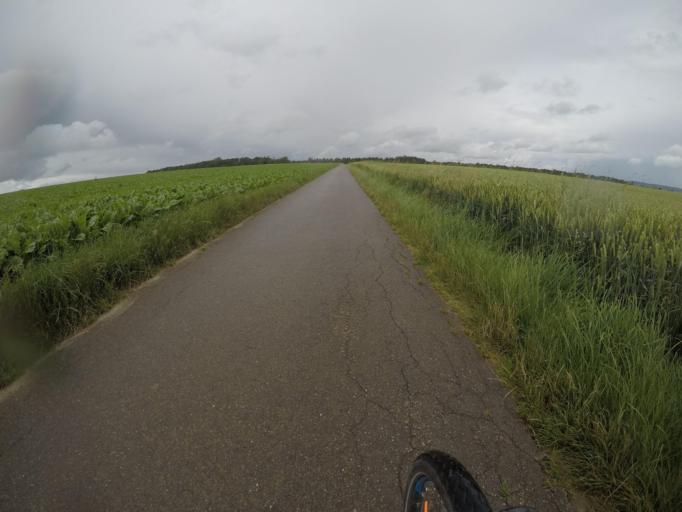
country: DE
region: Baden-Wuerttemberg
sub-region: Regierungsbezirk Stuttgart
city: Bondorf
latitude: 48.5611
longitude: 8.8289
